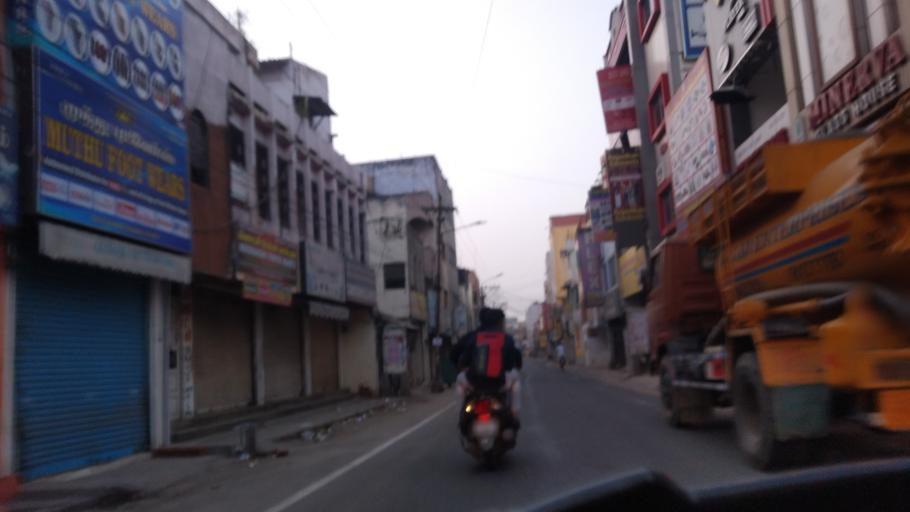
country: IN
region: Tamil Nadu
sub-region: Coimbatore
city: Coimbatore
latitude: 10.9970
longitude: 76.9602
